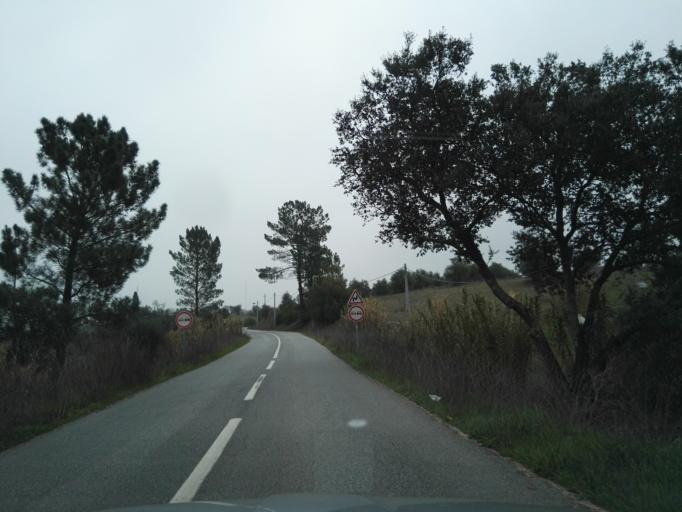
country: PT
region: Evora
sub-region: Vendas Novas
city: Vendas Novas
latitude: 38.7708
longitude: -8.3742
